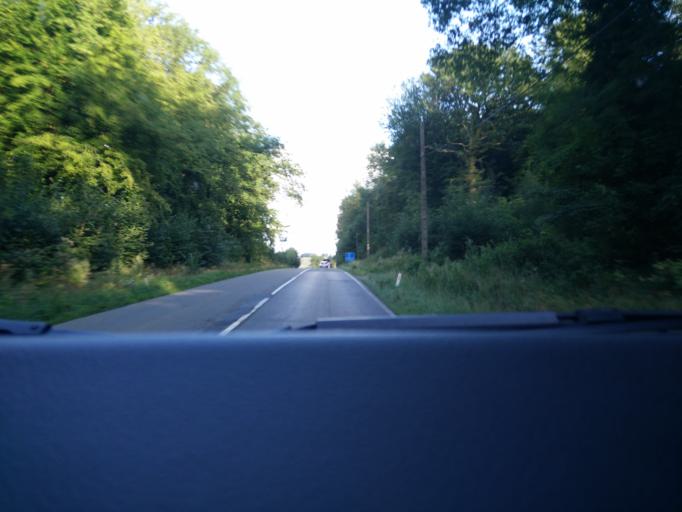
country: BE
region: Wallonia
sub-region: Province de Namur
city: Philippeville
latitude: 50.2026
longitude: 4.4898
